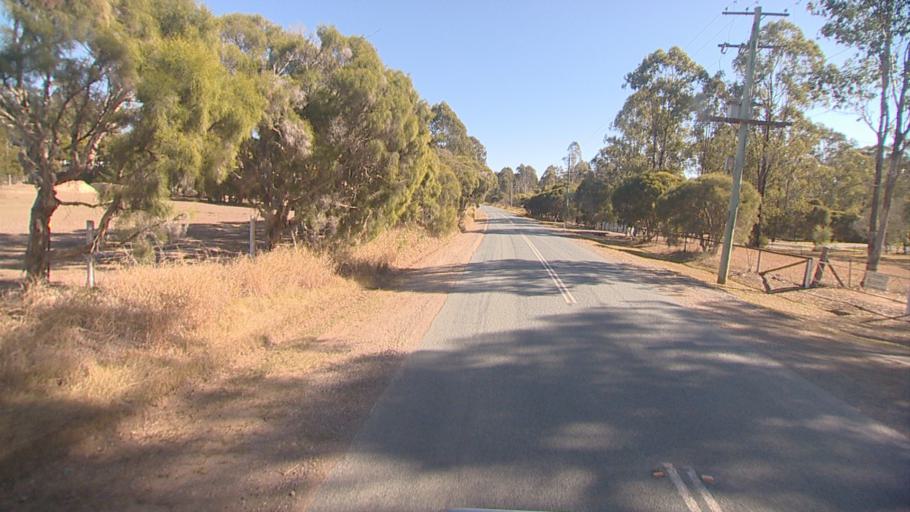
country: AU
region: Queensland
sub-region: Logan
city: Cedar Vale
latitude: -27.8507
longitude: 153.0411
